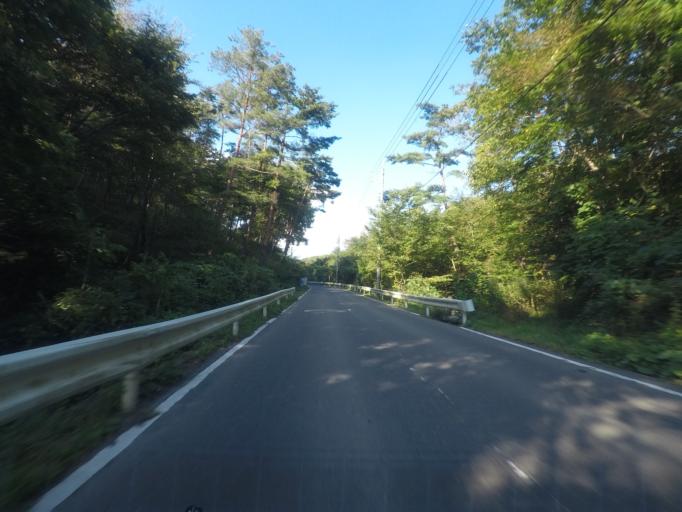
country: JP
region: Fukushima
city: Fukushima-shi
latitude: 37.7163
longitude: 140.5135
